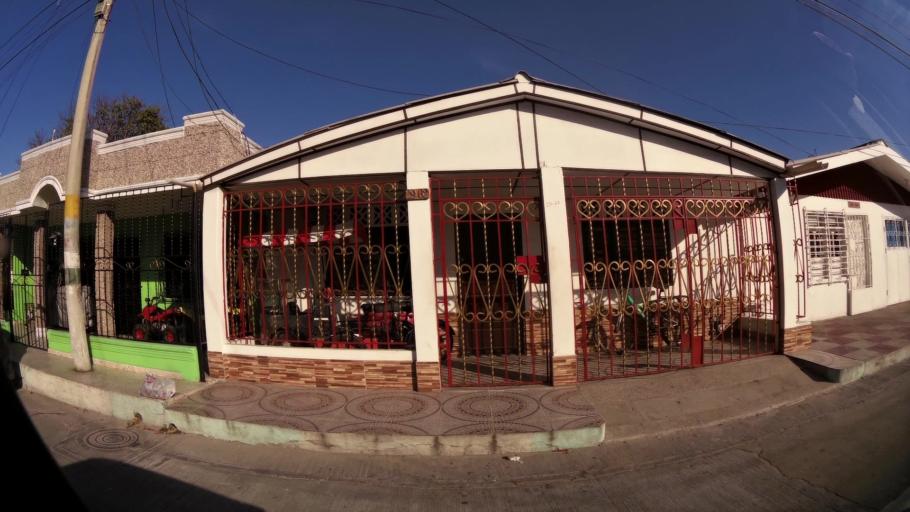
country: CO
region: Atlantico
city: Barranquilla
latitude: 10.9690
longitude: -74.7831
